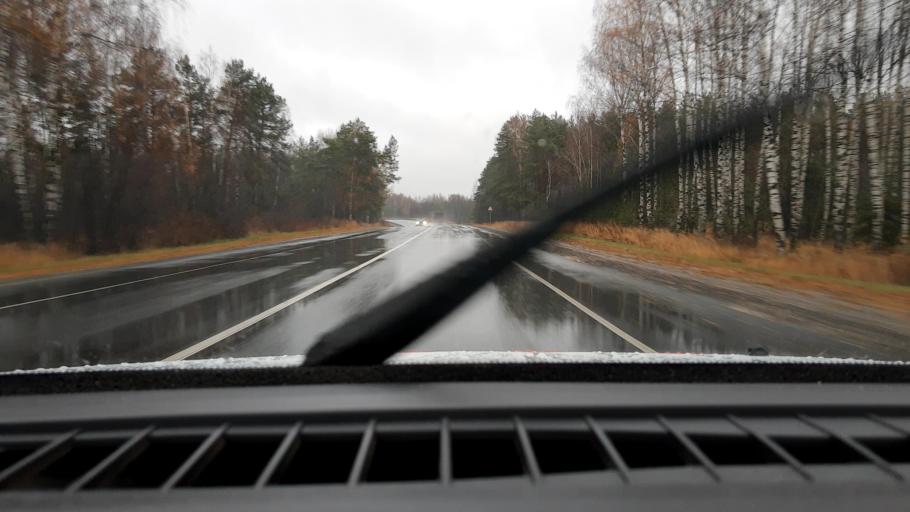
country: RU
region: Nizjnij Novgorod
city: Linda
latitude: 56.6586
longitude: 44.1251
